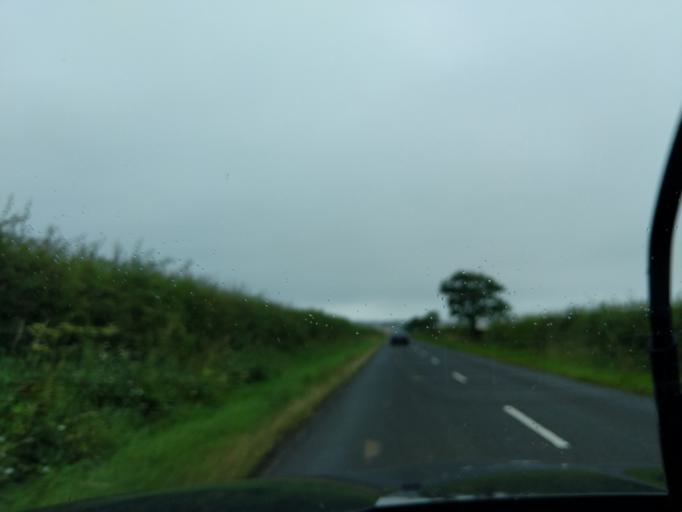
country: GB
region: England
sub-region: Northumberland
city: Lowick
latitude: 55.6591
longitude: -1.9405
